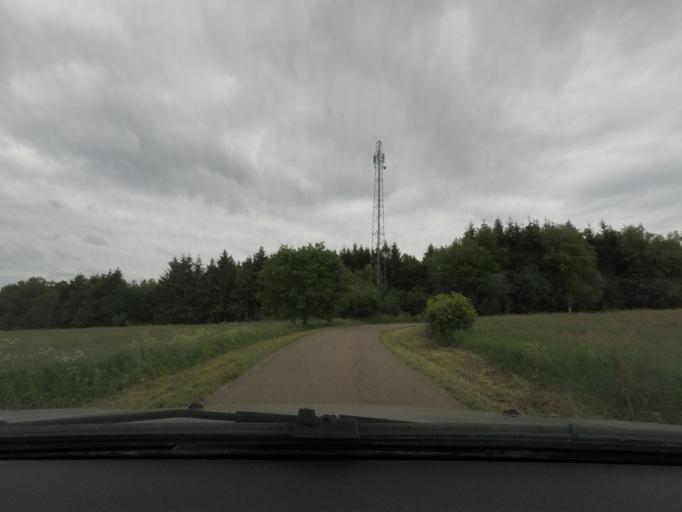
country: BE
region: Wallonia
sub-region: Province du Luxembourg
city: Leglise
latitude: 49.8287
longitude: 5.5168
